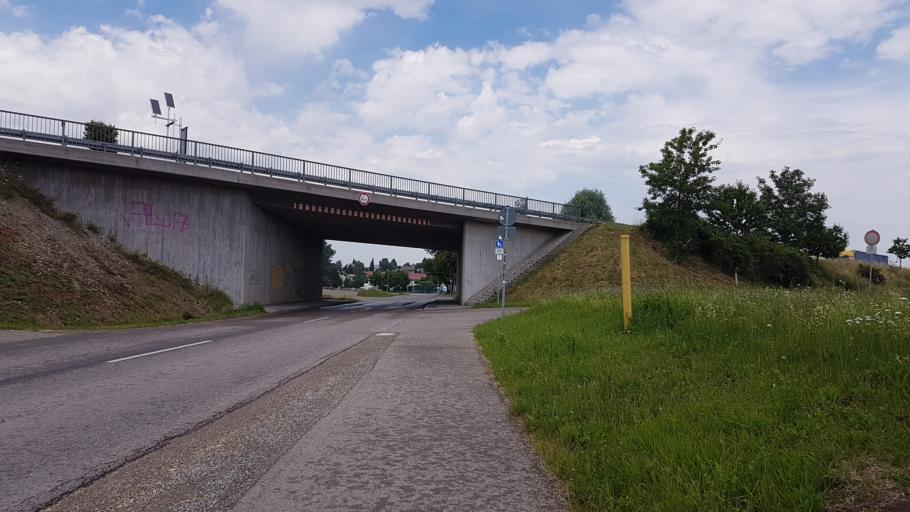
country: DE
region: Baden-Wuerttemberg
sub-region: Freiburg Region
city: Hufingen
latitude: 47.9174
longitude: 8.4914
